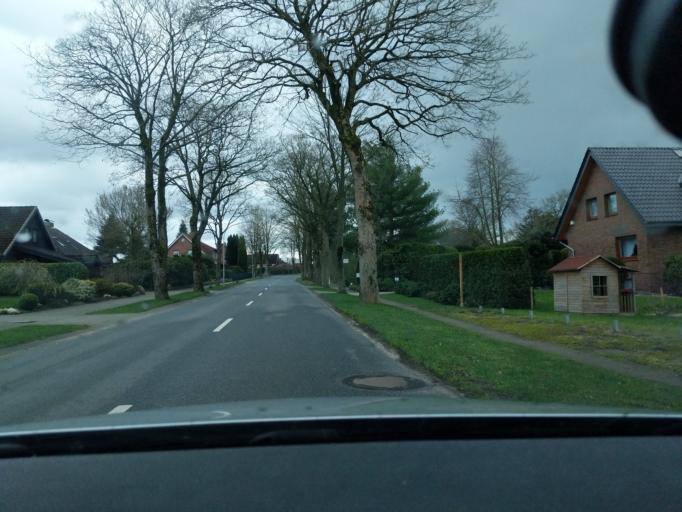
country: DE
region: Lower Saxony
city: Kutenholz
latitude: 53.5065
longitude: 9.3031
